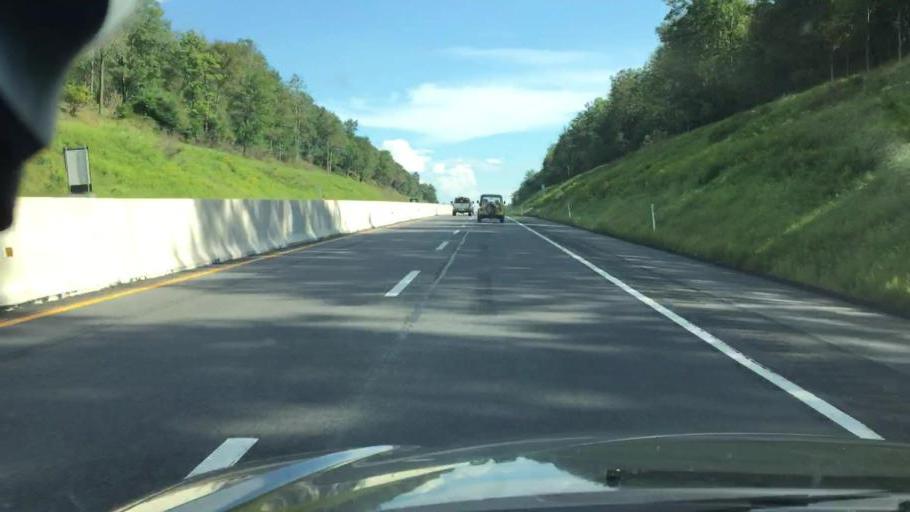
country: US
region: Pennsylvania
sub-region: Luzerne County
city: White Haven
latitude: 41.0625
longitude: -75.6878
